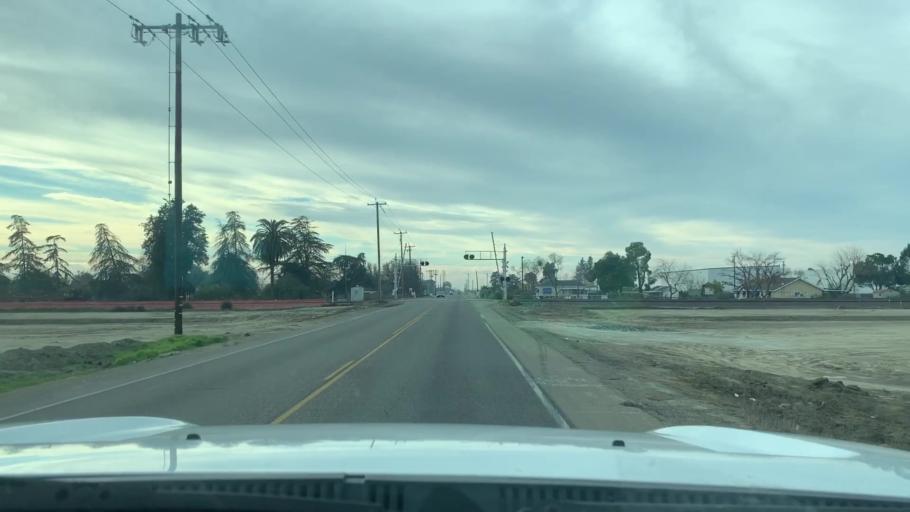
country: US
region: California
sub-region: Fresno County
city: Easton
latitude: 36.6054
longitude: -119.7492
